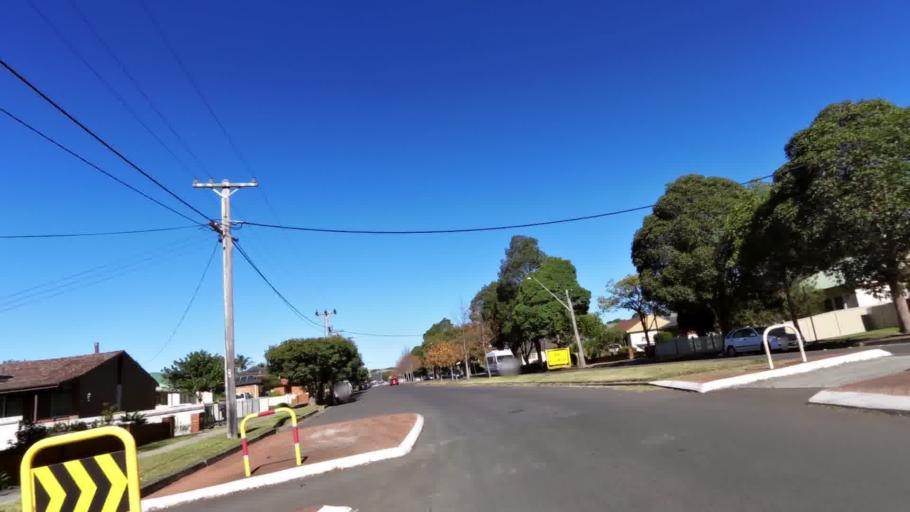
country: AU
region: New South Wales
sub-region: Shellharbour
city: Albion Park Rail
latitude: -34.5591
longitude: 150.8186
